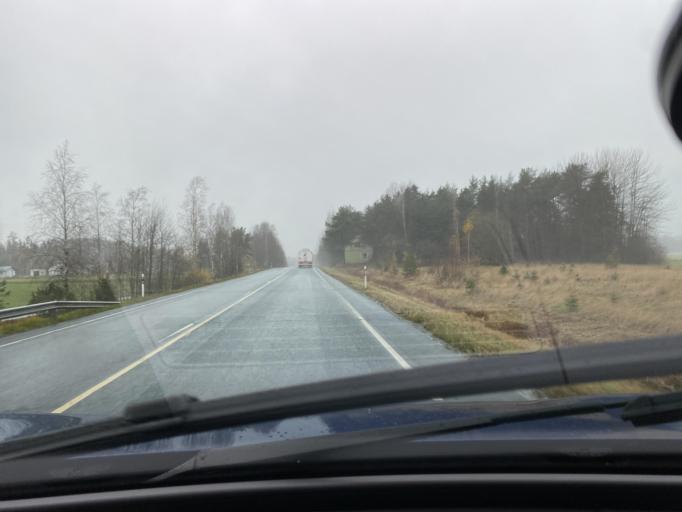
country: FI
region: Haeme
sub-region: Forssa
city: Jokioinen
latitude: 60.7767
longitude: 23.3859
